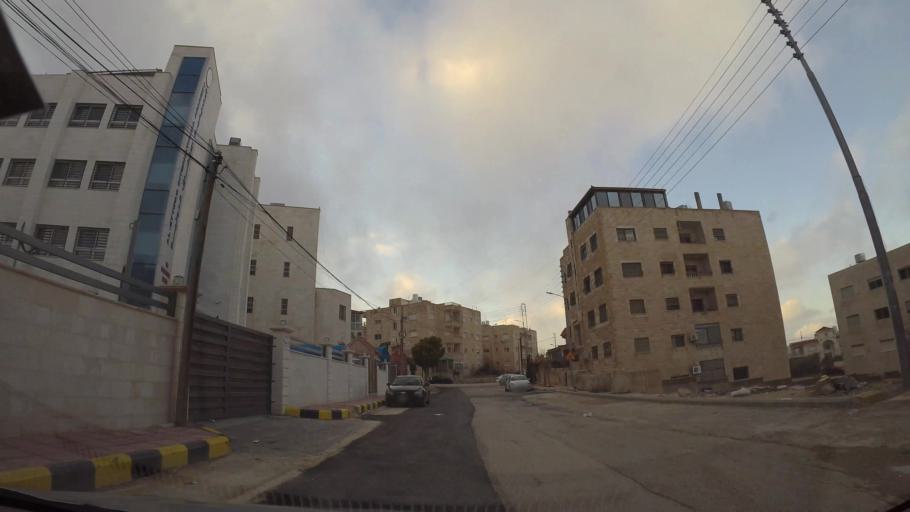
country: JO
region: Amman
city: Al Jubayhah
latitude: 32.0484
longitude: 35.8968
